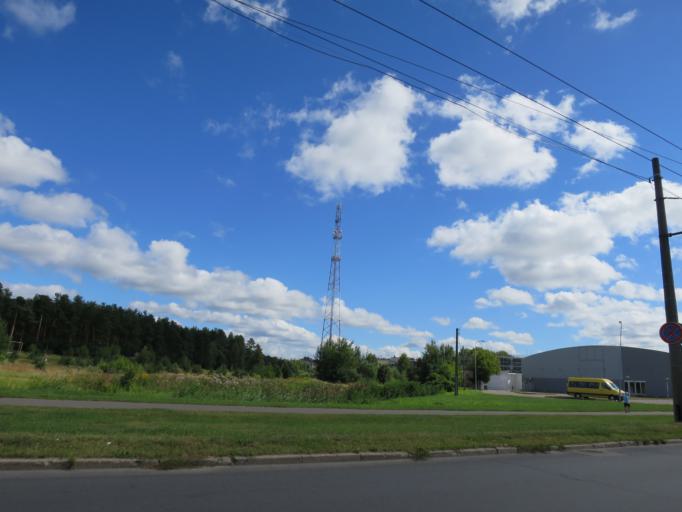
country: LV
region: Stopini
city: Ulbroka
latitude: 56.9611
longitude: 24.2385
